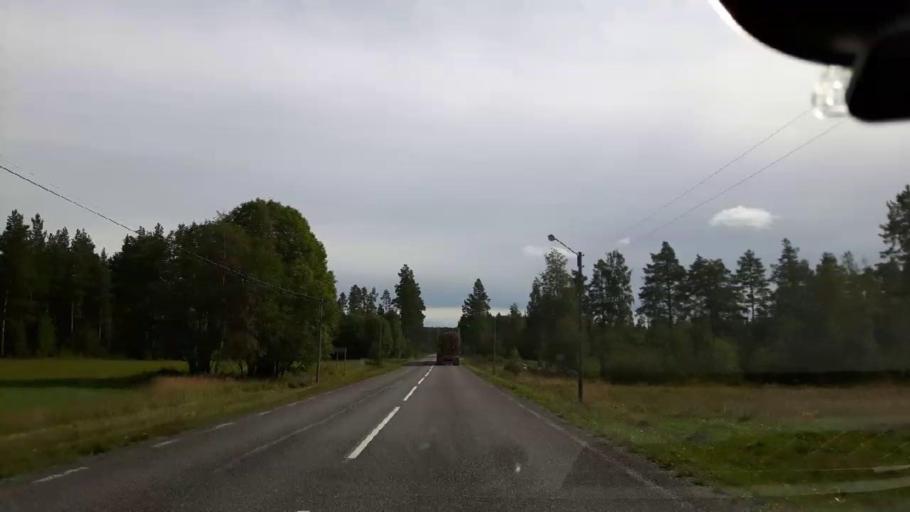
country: SE
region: Jaemtland
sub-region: Ragunda Kommun
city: Hammarstrand
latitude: 63.1476
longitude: 15.8445
